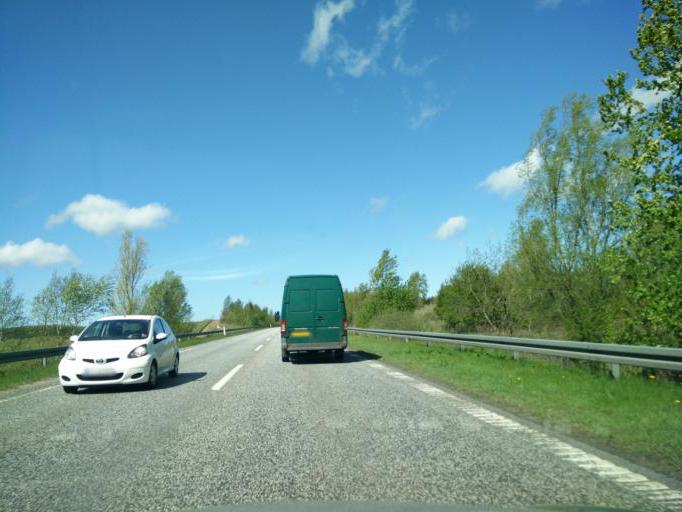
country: DK
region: Capital Region
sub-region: Hillerod Kommune
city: Hillerod
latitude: 55.9674
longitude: 12.2445
